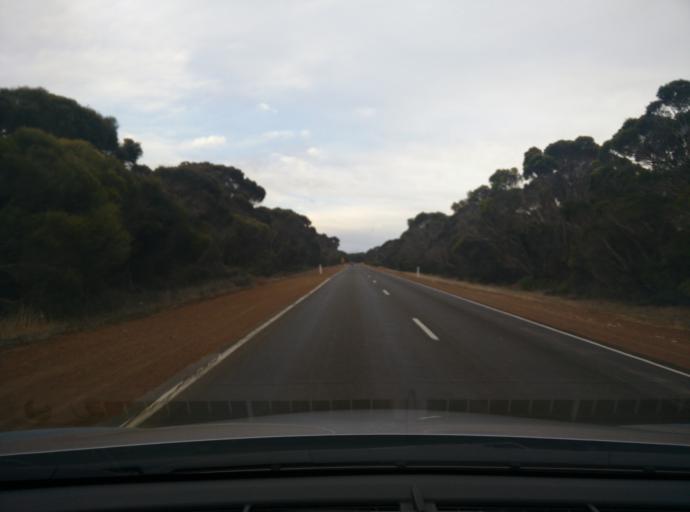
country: AU
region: South Australia
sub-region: Kangaroo Island
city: Kingscote
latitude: -35.7225
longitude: 137.5601
